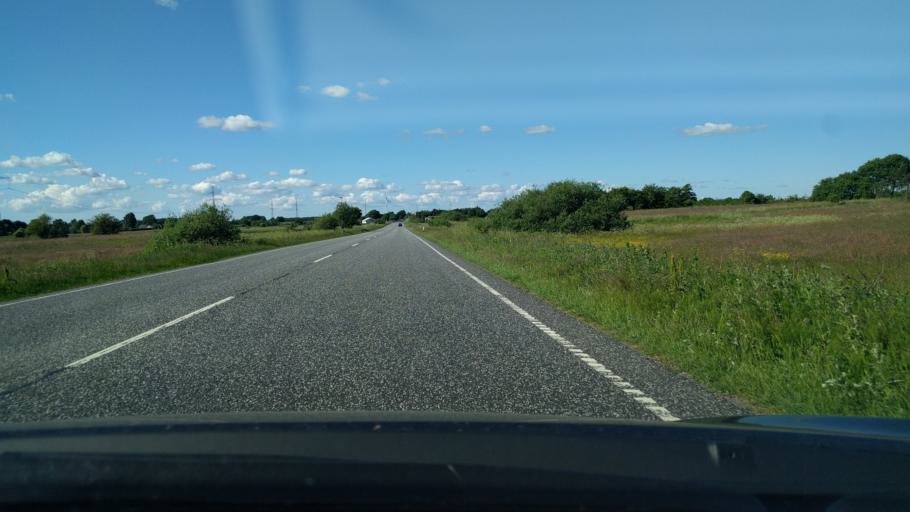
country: DK
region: North Denmark
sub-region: Vesthimmerland Kommune
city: Alestrup
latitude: 56.6584
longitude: 9.5214
